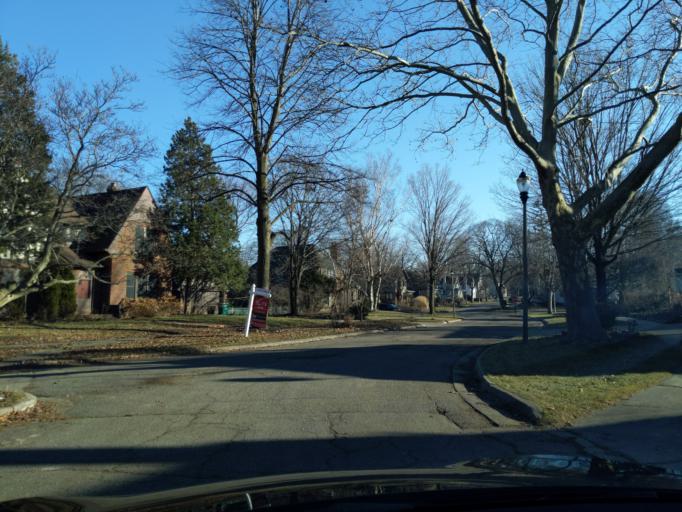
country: US
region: Michigan
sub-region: Ingham County
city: Lansing
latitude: 42.7382
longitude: -84.5702
